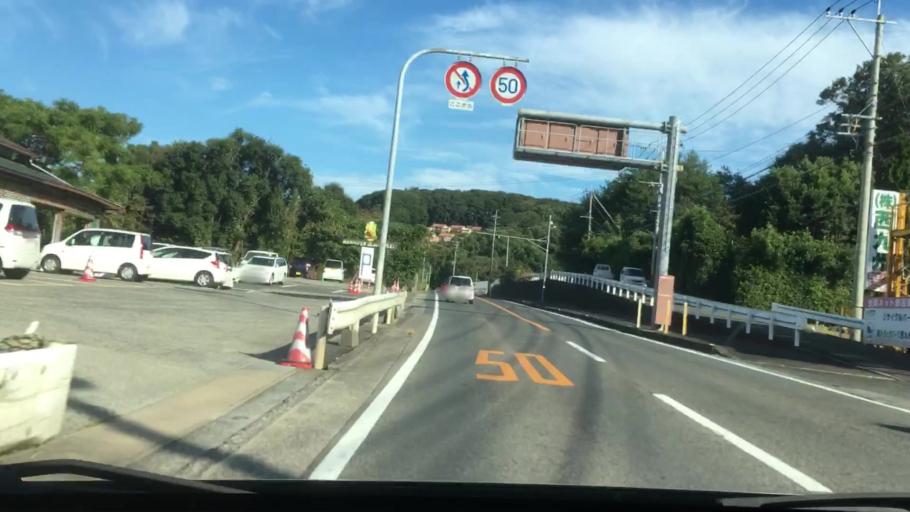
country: JP
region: Nagasaki
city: Sasebo
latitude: 33.0663
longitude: 129.7642
